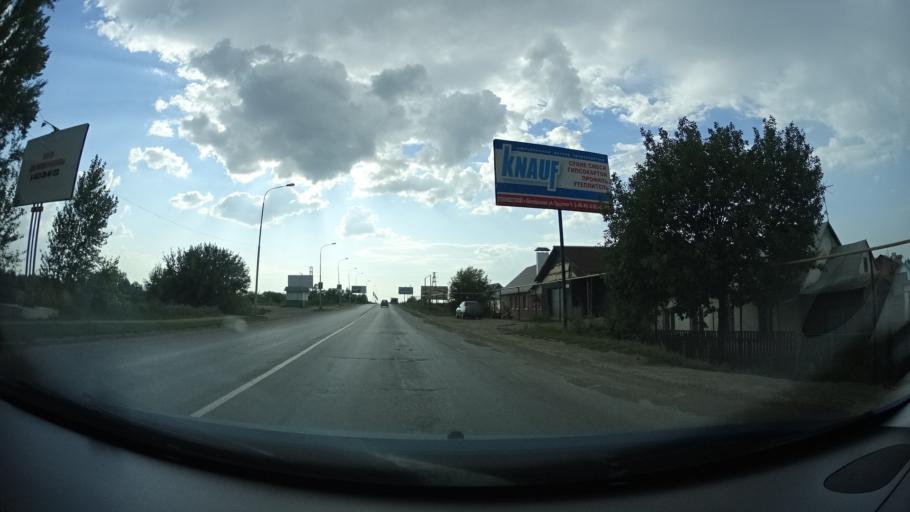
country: RU
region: Bashkortostan
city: Oktyabr'skiy
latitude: 54.4849
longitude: 53.4394
